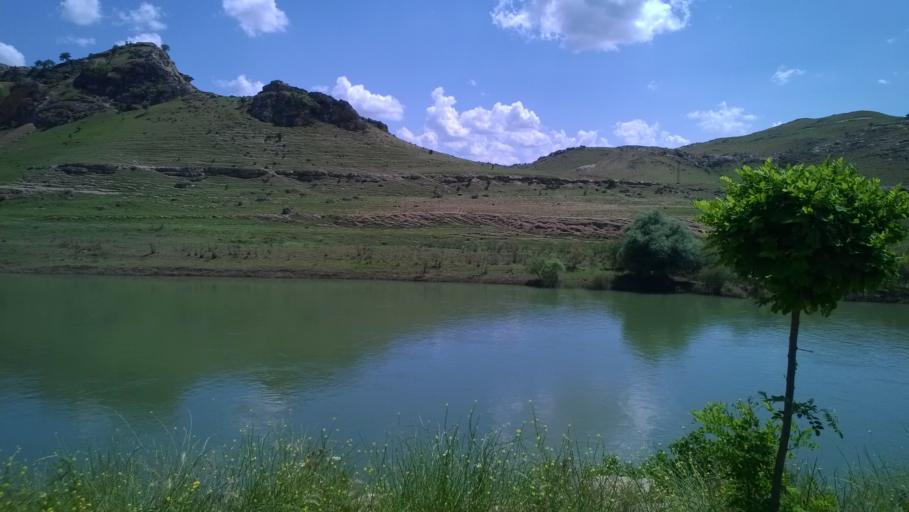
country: TR
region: Batman
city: Oymatas
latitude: 37.7672
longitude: 41.0687
